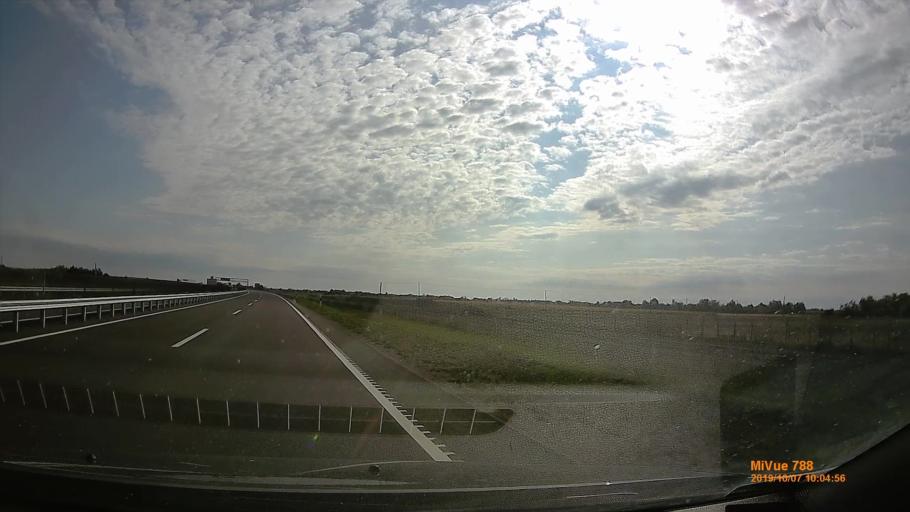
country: HU
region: Bekes
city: Kondoros
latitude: 46.7383
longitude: 20.7880
